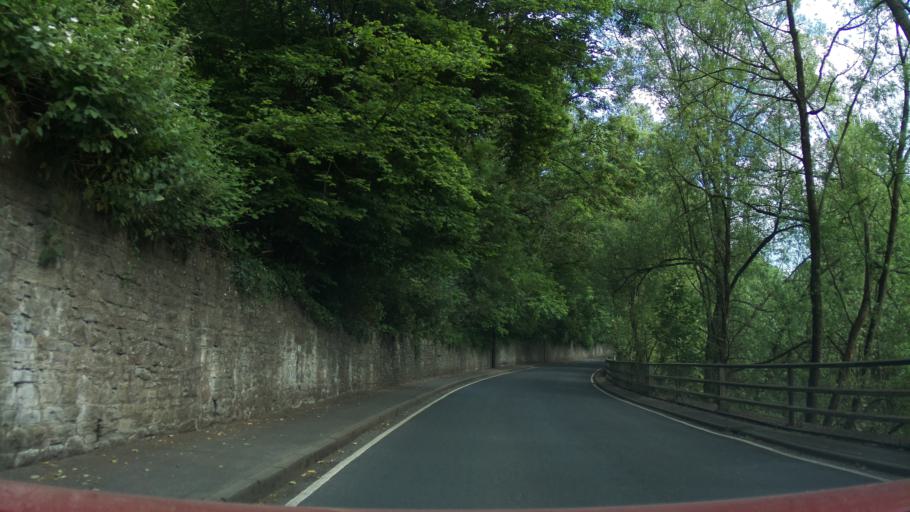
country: GB
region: England
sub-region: South Gloucestershire
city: Kingswood
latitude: 51.4496
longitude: -2.5342
